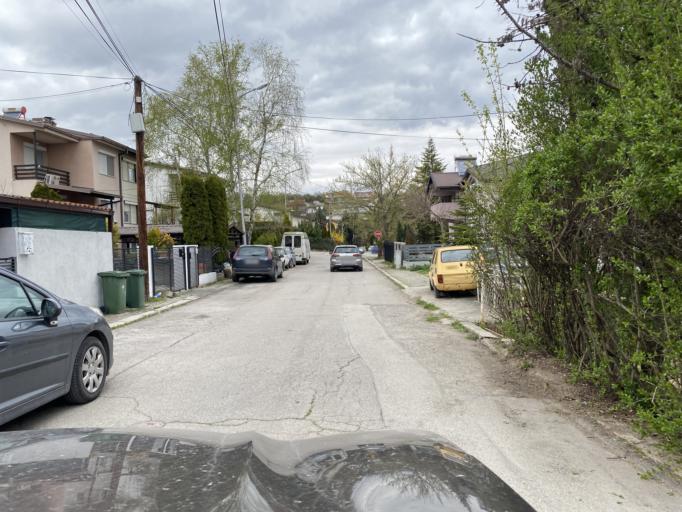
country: MK
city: Radishani
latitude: 42.0646
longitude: 21.4492
